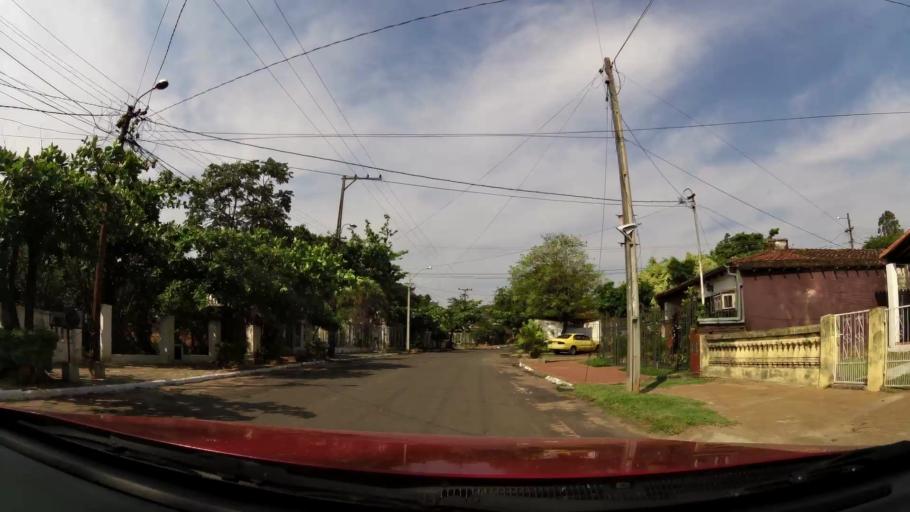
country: PY
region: Central
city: Fernando de la Mora
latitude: -25.2715
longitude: -57.5505
